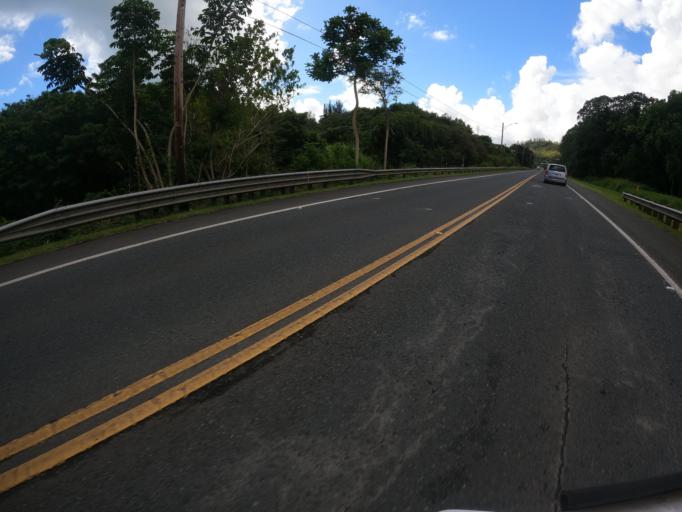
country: US
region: Hawaii
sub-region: Honolulu County
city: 'Ahuimanu
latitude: 21.4408
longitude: -157.8315
